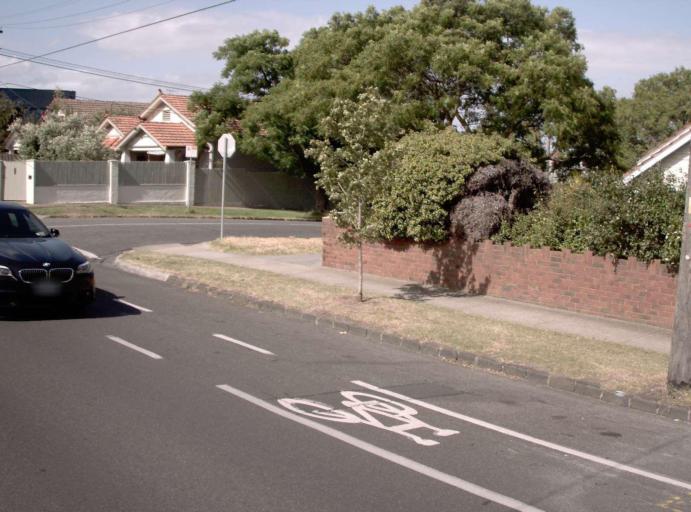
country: AU
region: Victoria
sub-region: Stonnington
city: Glen Iris
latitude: -37.8594
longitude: 145.0410
